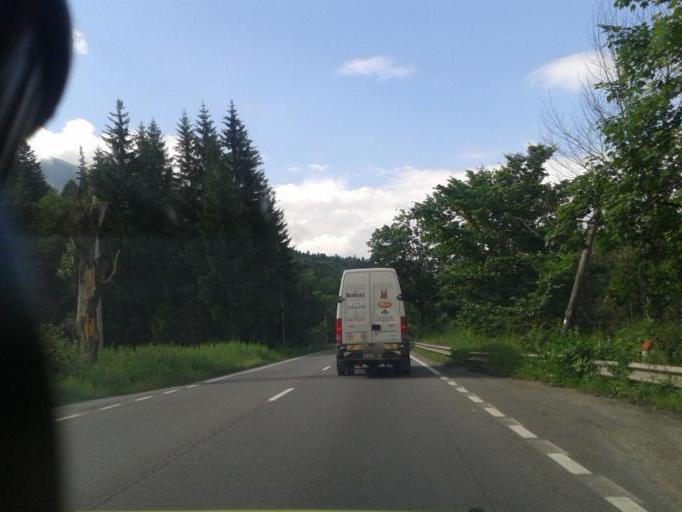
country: RO
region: Prahova
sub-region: Oras Busteni
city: Poiana Tapului
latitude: 45.3788
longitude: 25.5392
